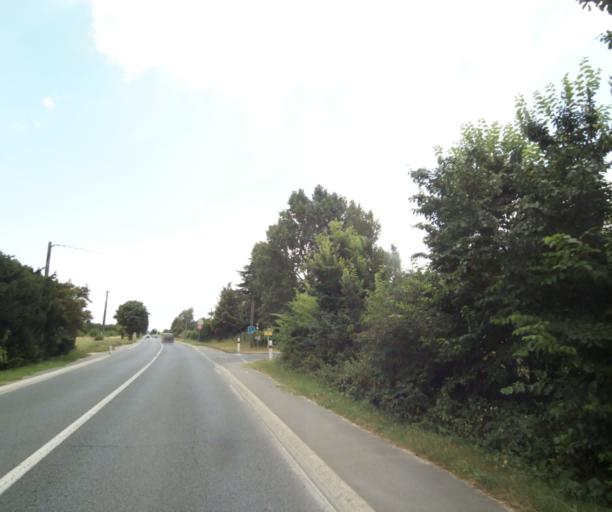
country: FR
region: Centre
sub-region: Departement du Loiret
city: Saint-Jean-de-Braye
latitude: 47.9034
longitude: 1.9959
